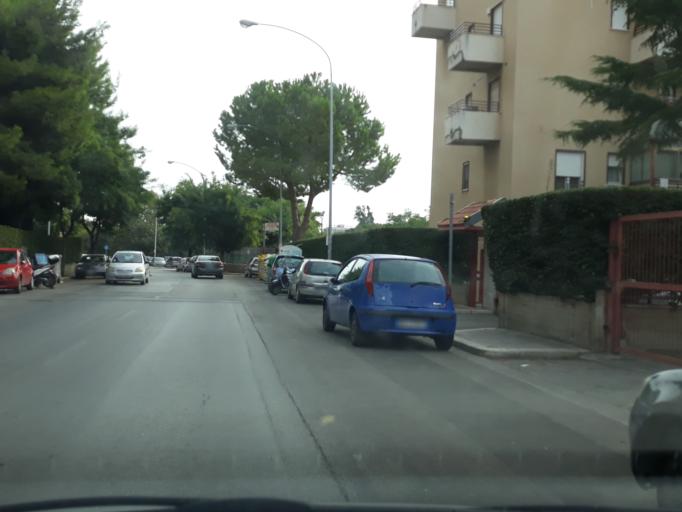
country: IT
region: Sicily
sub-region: Palermo
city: Palermo
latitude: 38.0998
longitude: 13.3257
